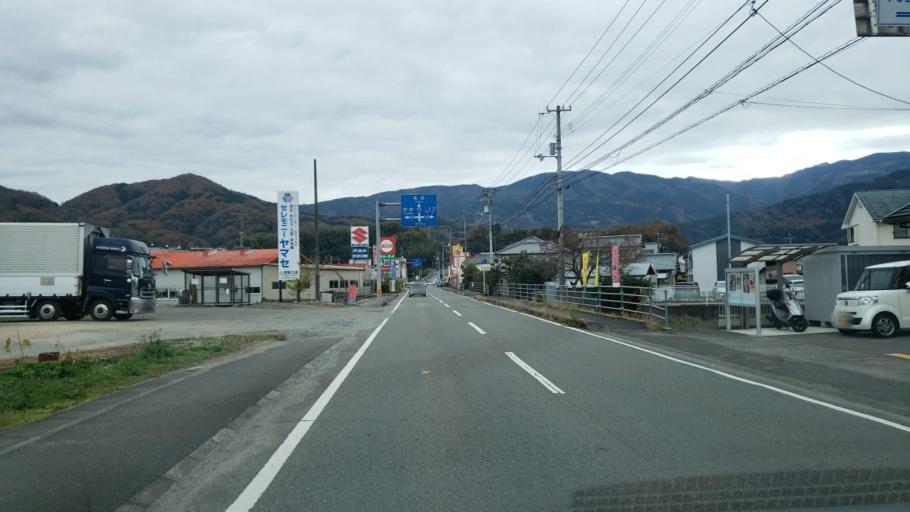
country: JP
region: Tokushima
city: Wakimachi
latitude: 34.0600
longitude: 134.2383
